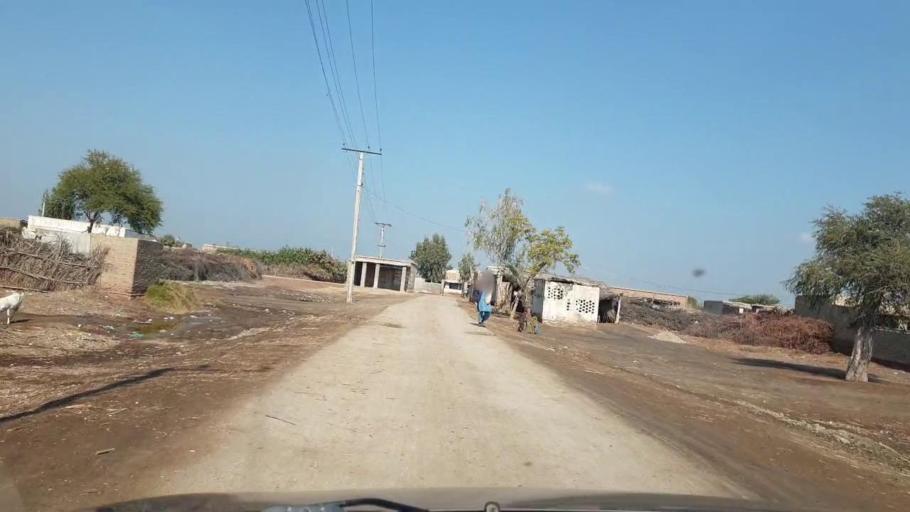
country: PK
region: Sindh
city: Sinjhoro
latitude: 26.0605
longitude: 68.7564
